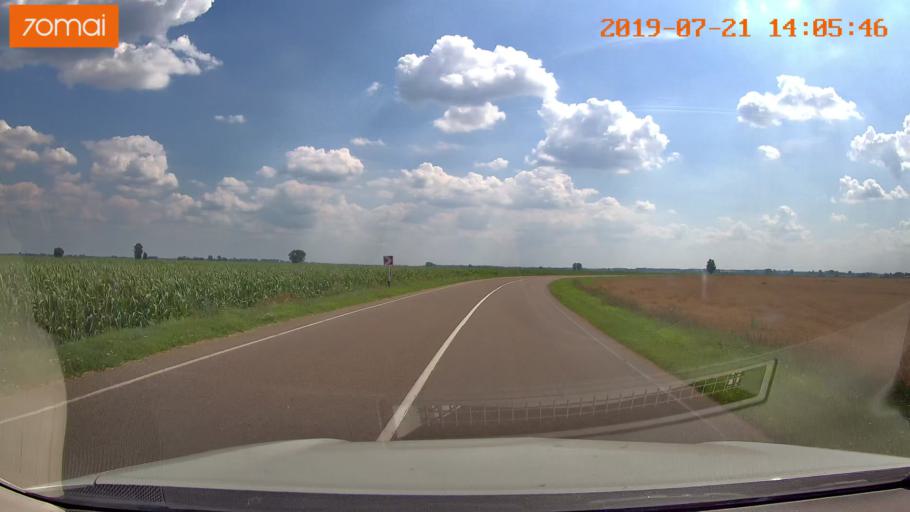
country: BY
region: Grodnenskaya
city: Lyubcha
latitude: 53.7068
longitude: 26.1110
